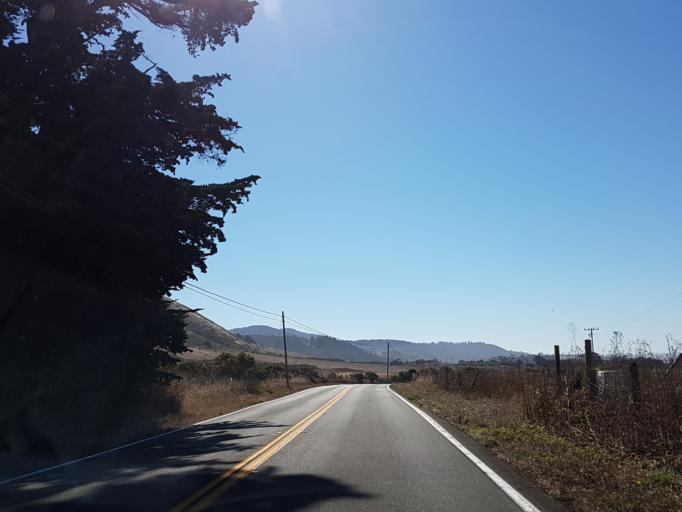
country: US
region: California
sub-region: Mendocino County
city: Boonville
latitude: 39.0772
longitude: -123.6947
